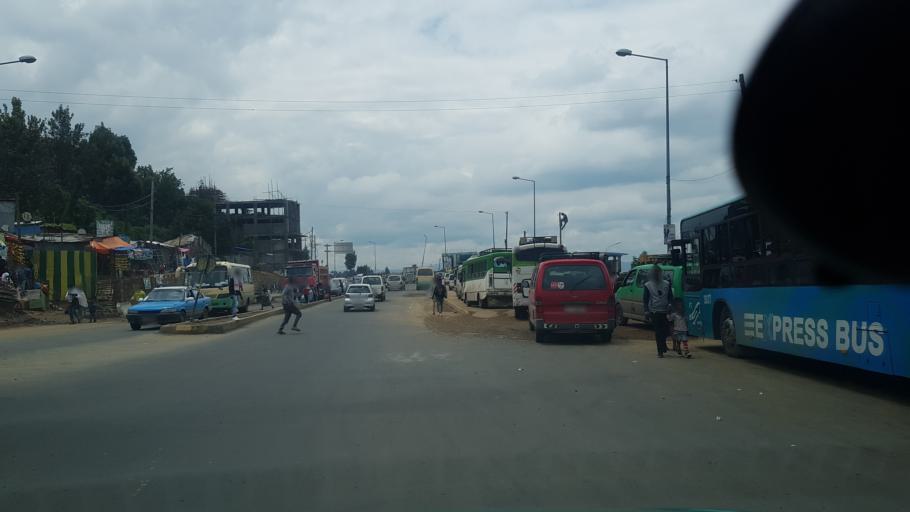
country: ET
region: Adis Abeba
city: Addis Ababa
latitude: 9.0211
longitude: 38.8019
